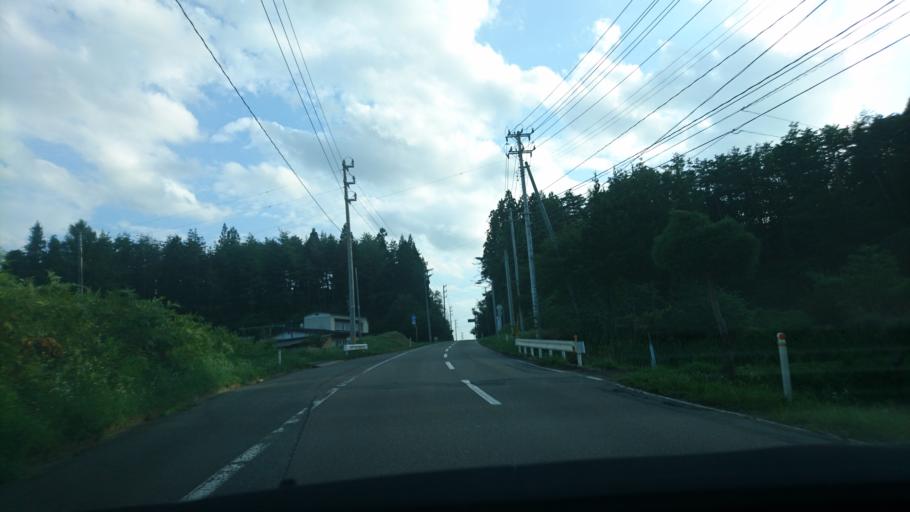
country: JP
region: Iwate
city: Ichinoseki
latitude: 39.0105
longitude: 141.2867
